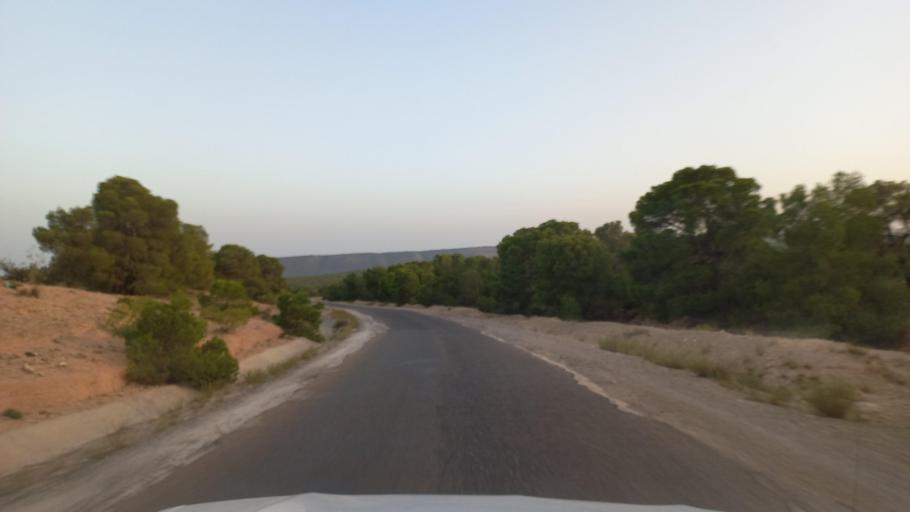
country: TN
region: Al Qasrayn
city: Sbiba
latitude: 35.4207
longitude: 8.9241
